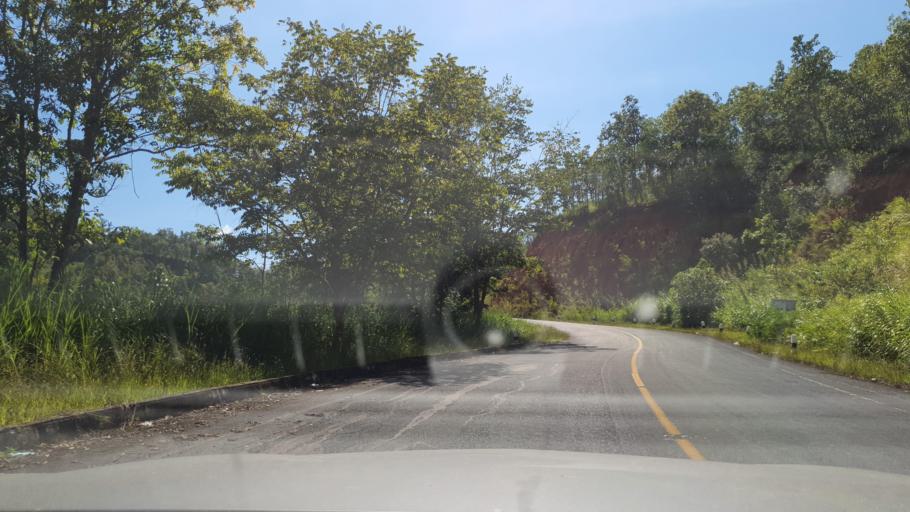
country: TH
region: Chiang Mai
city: Phrao
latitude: 19.3595
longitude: 99.2748
